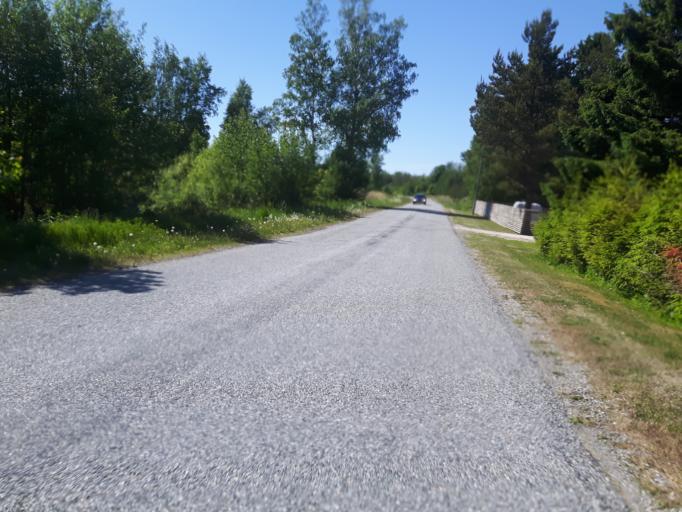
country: EE
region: Laeaene-Virumaa
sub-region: Haljala vald
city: Haljala
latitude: 59.5655
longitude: 26.3078
